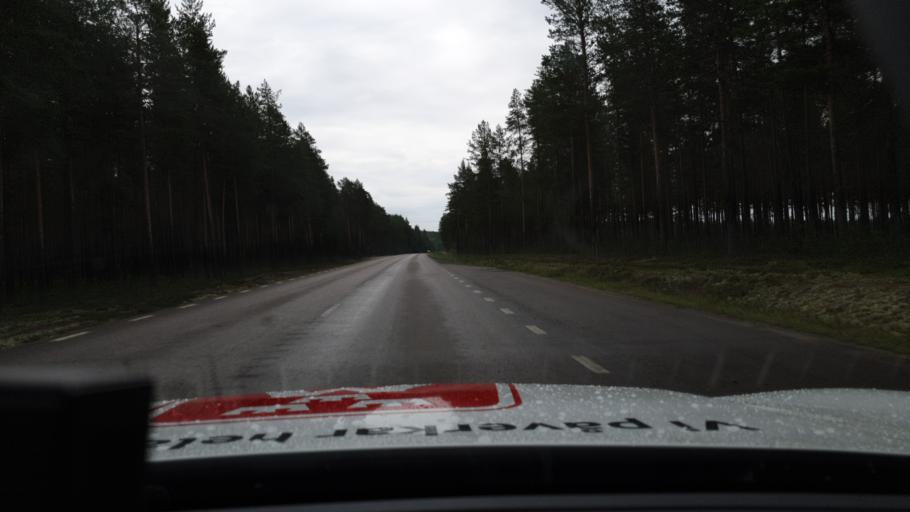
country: SE
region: Norrbotten
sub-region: Alvsbyns Kommun
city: AElvsbyn
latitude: 66.1375
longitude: 20.8922
